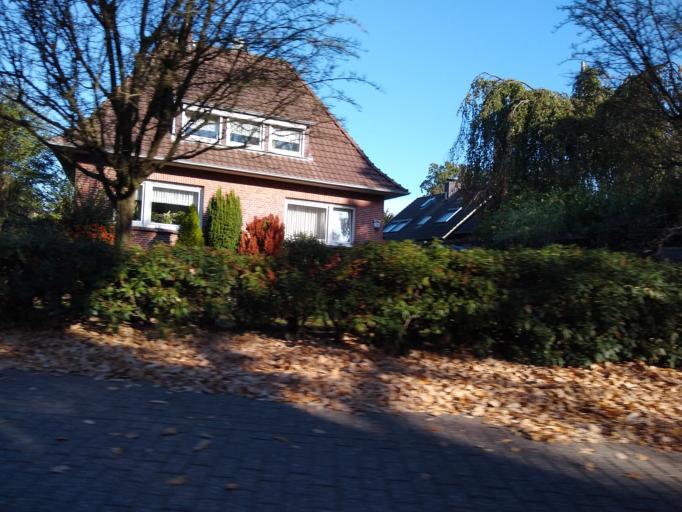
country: DE
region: Lower Saxony
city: Oldenburg
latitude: 53.1859
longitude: 8.2123
